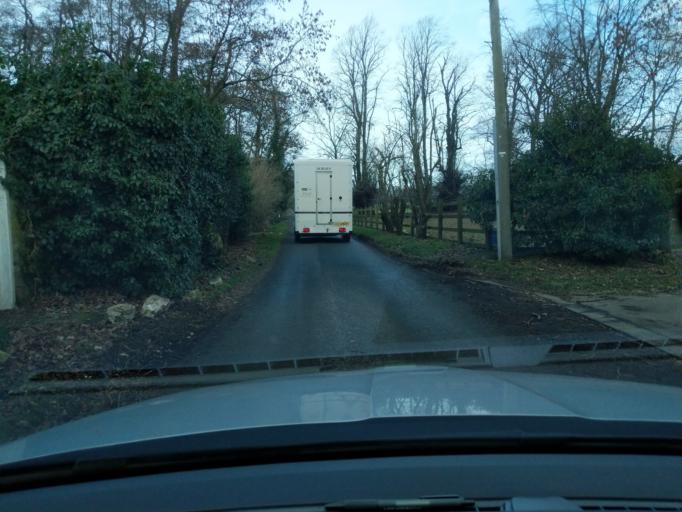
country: GB
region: England
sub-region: North Yorkshire
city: Catterick
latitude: 54.3686
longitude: -1.6694
